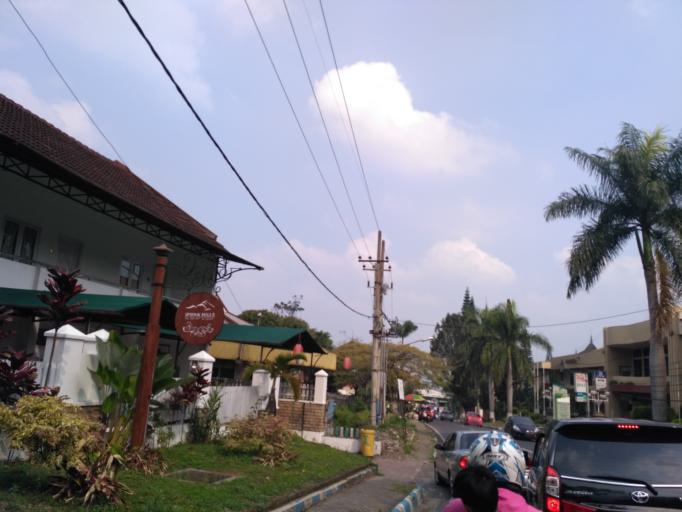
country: ID
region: East Java
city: Batu
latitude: -7.8398
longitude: 112.5281
